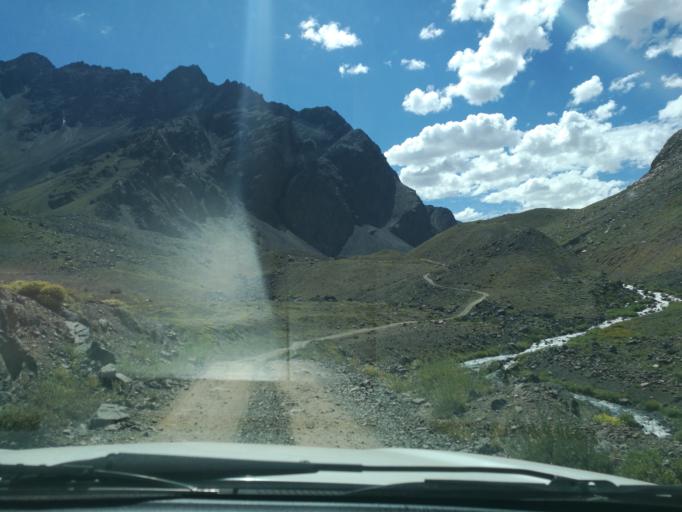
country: CL
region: O'Higgins
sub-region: Provincia de Cachapoal
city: Machali
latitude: -34.4142
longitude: -70.2236
